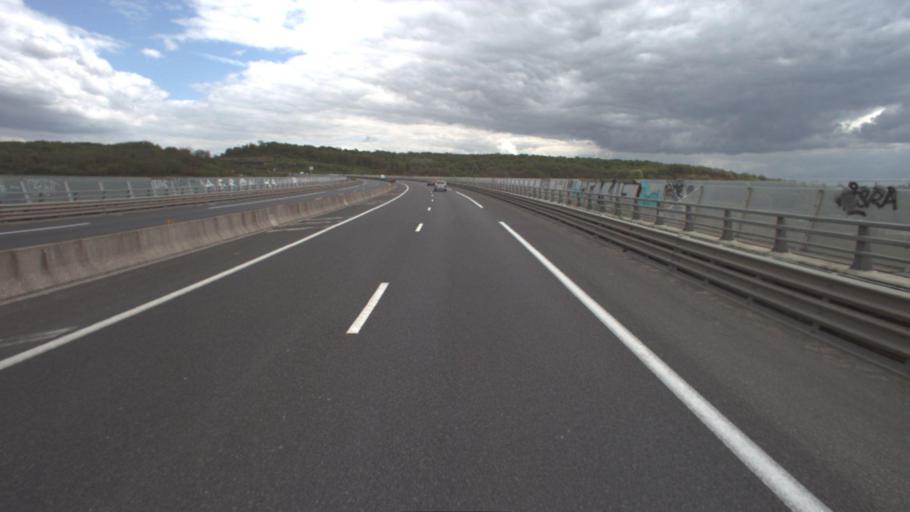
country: FR
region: Ile-de-France
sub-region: Departement de Seine-et-Marne
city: Mareuil-les-Meaux
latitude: 48.9172
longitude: 2.8517
